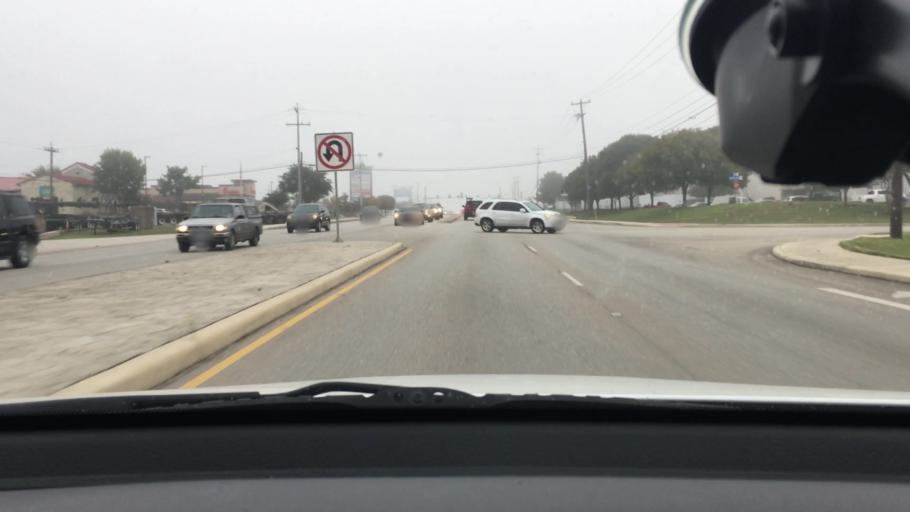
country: US
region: Texas
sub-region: Bexar County
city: Selma
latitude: 29.6057
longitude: -98.2804
